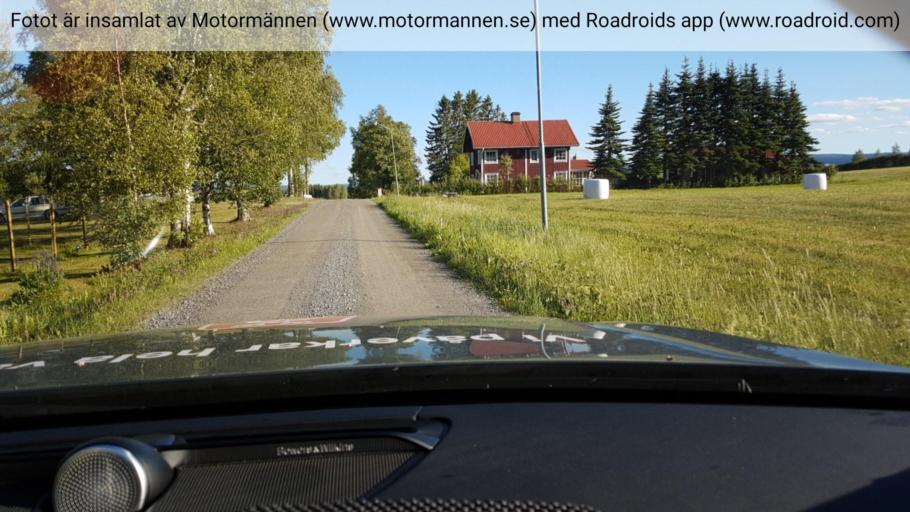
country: SE
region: Jaemtland
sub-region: Bergs Kommun
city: Hoverberg
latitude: 63.0102
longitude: 14.3448
